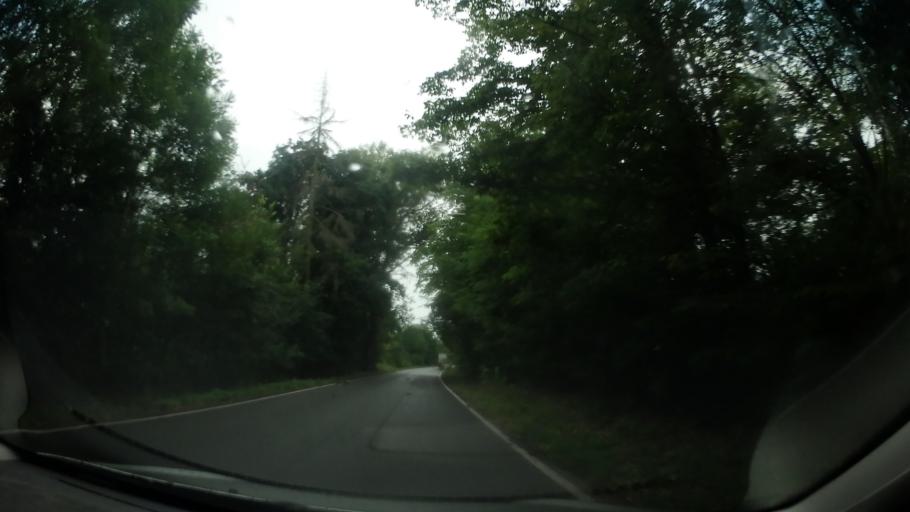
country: CZ
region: Central Bohemia
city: Milovice
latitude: 50.2439
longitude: 14.9202
